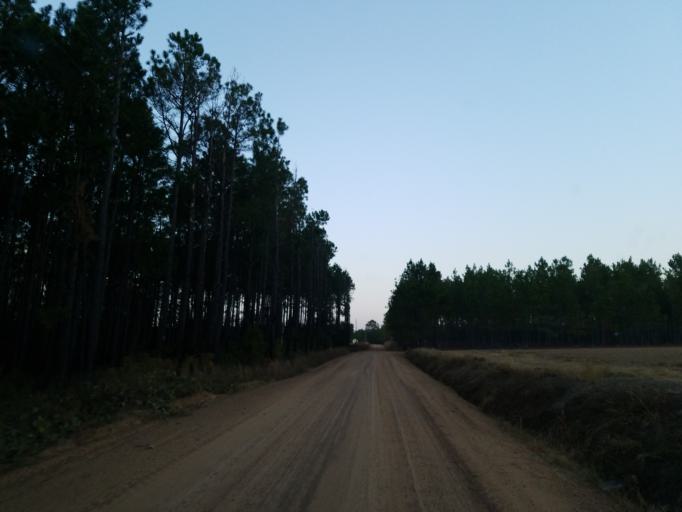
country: US
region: Georgia
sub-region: Turner County
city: Ashburn
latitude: 31.7359
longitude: -83.4845
